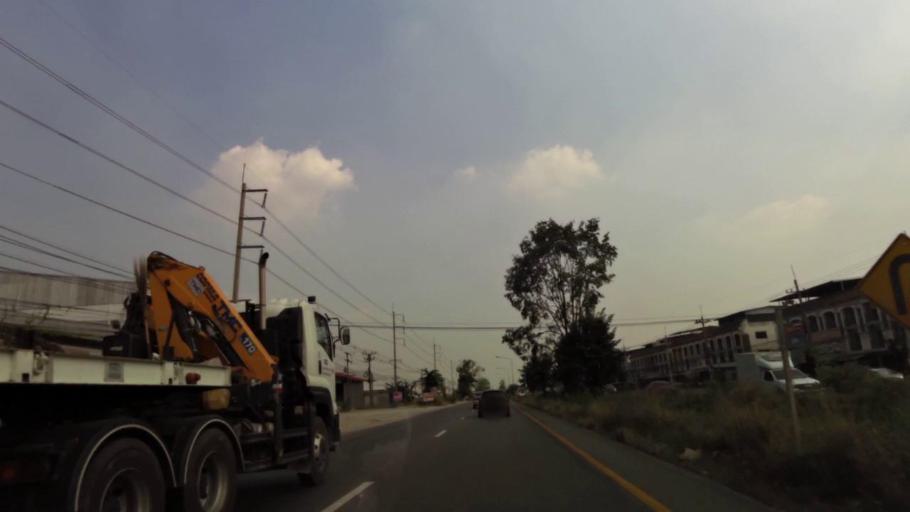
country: TH
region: Chon Buri
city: Ban Bueng
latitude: 13.3039
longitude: 101.1367
